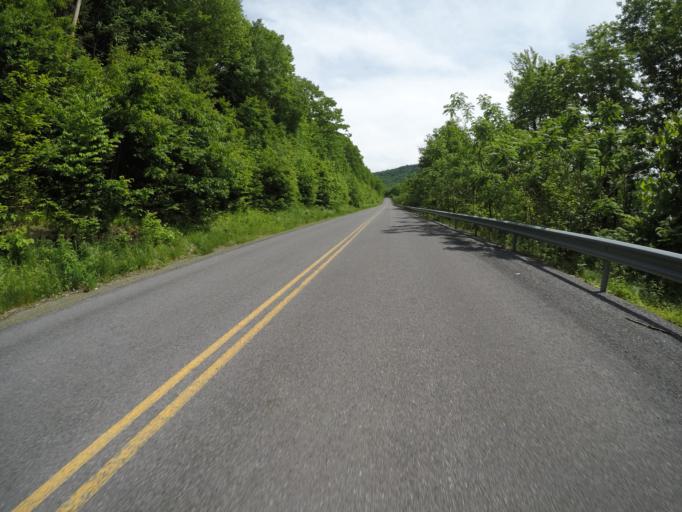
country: US
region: New York
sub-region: Sullivan County
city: Livingston Manor
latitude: 42.0995
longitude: -74.8258
